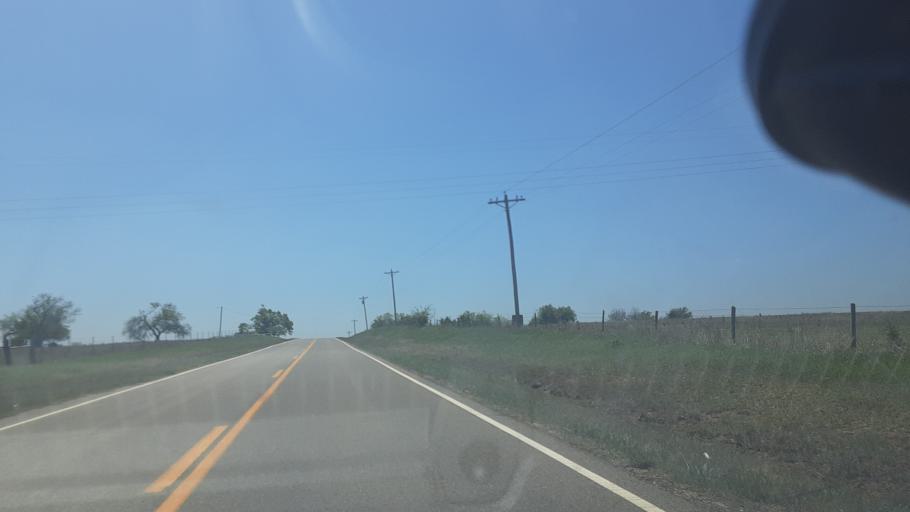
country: US
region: Oklahoma
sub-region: Logan County
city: Guthrie
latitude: 36.0217
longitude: -97.4076
